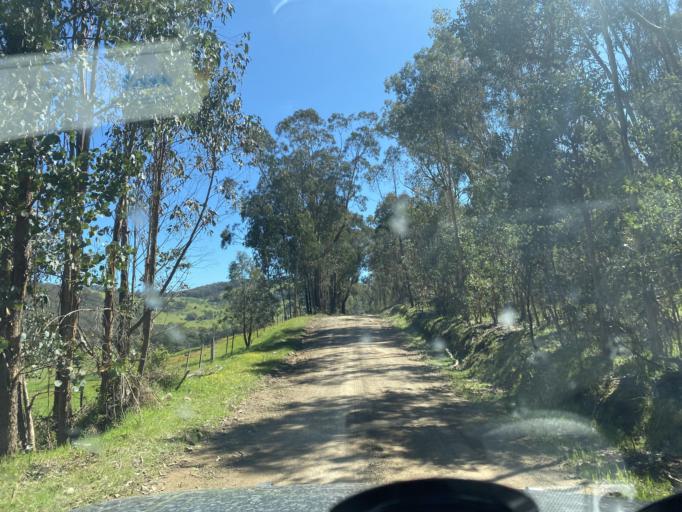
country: AU
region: Victoria
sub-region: Benalla
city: Benalla
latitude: -36.6940
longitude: 146.1767
